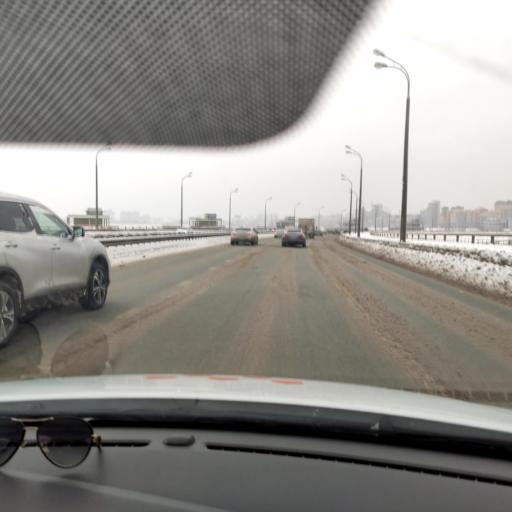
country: RU
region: Tatarstan
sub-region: Gorod Kazan'
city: Kazan
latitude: 55.8108
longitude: 49.1377
